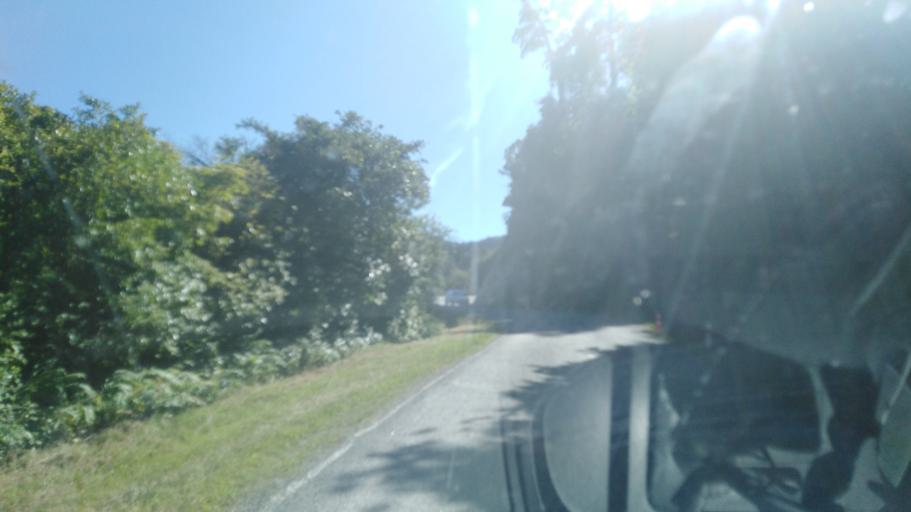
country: NZ
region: West Coast
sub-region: Buller District
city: Westport
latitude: -41.5269
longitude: 172.0009
